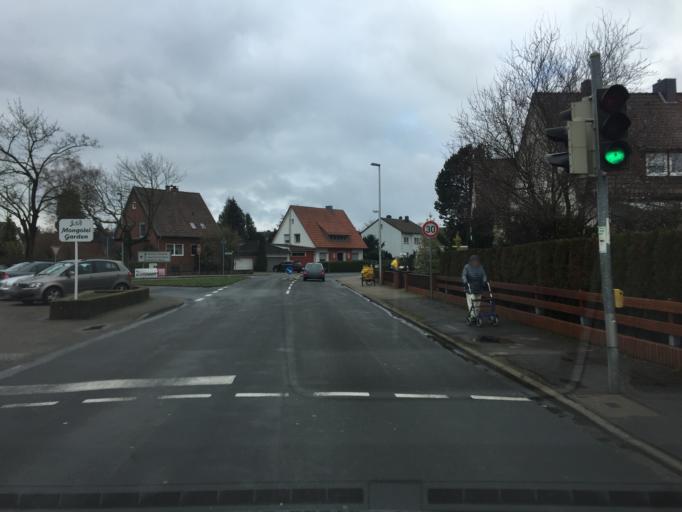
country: DE
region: Lower Saxony
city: Wunstorf
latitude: 52.4180
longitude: 9.4321
